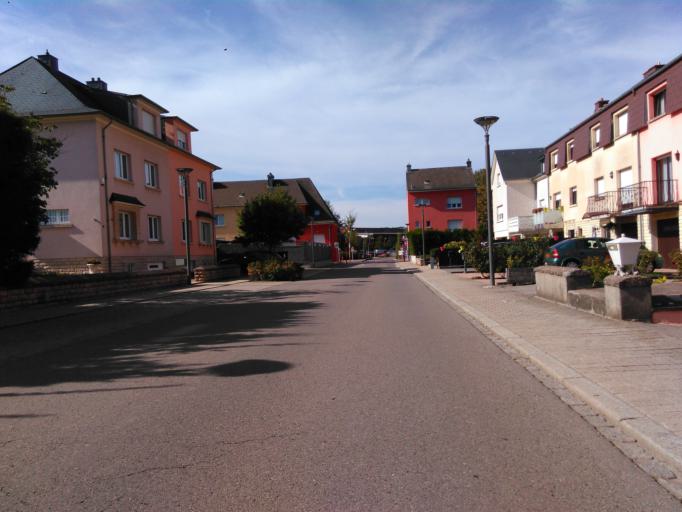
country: LU
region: Luxembourg
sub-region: Canton de Capellen
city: Bascharage
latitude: 49.5637
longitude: 5.9063
